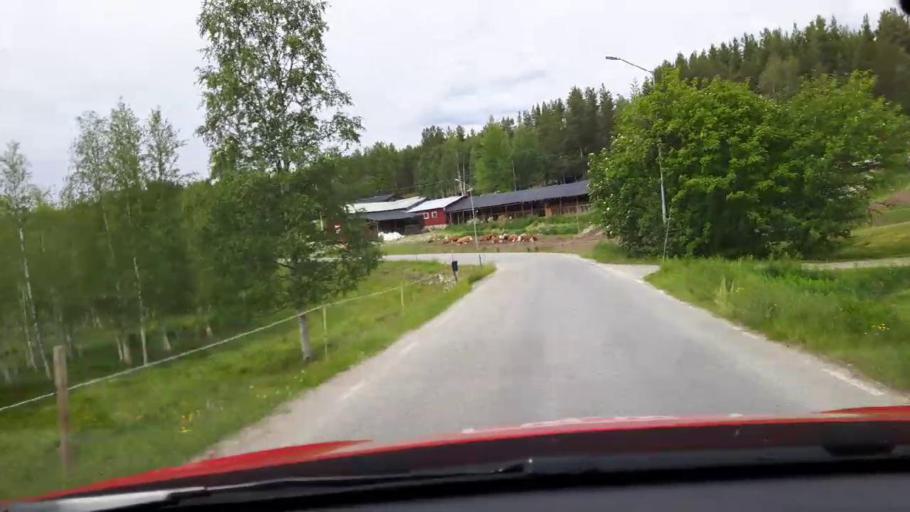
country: SE
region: Jaemtland
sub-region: Harjedalens Kommun
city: Sveg
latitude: 62.4105
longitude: 13.6707
